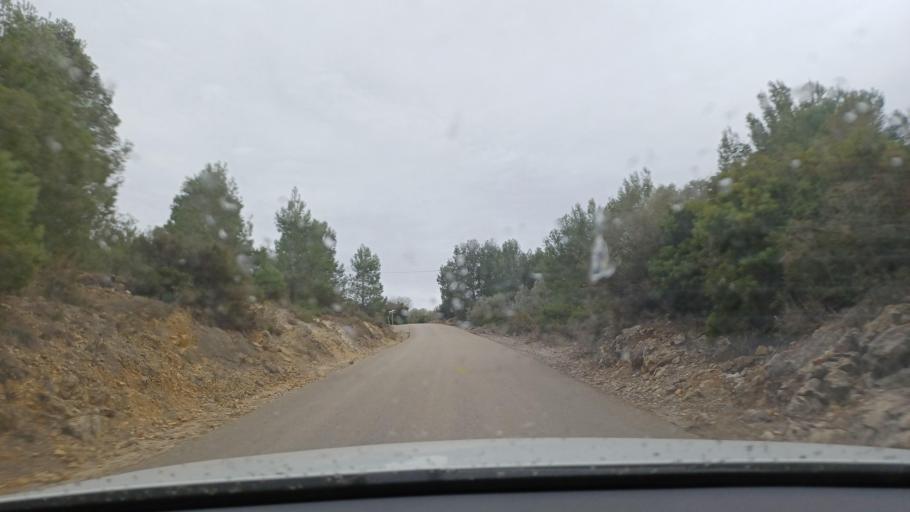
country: ES
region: Valencia
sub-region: Provincia de Castello
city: Traiguera
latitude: 40.5073
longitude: 0.2944
